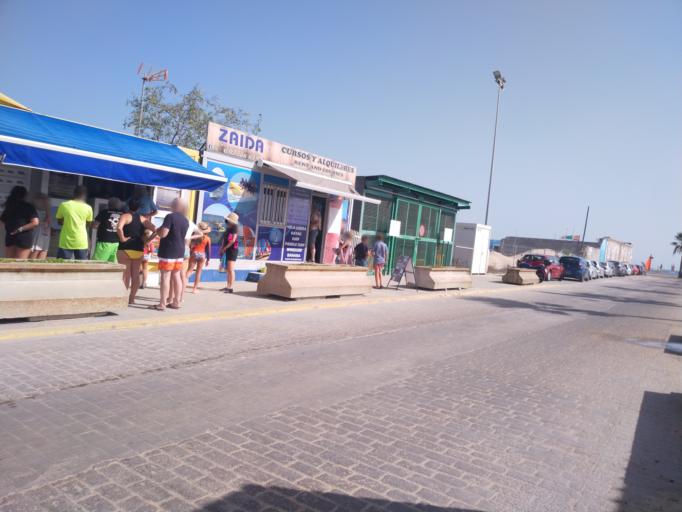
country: ES
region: Andalusia
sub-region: Provincia de Cadiz
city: Chiclana de la Frontera
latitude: 36.3944
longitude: -6.2087
